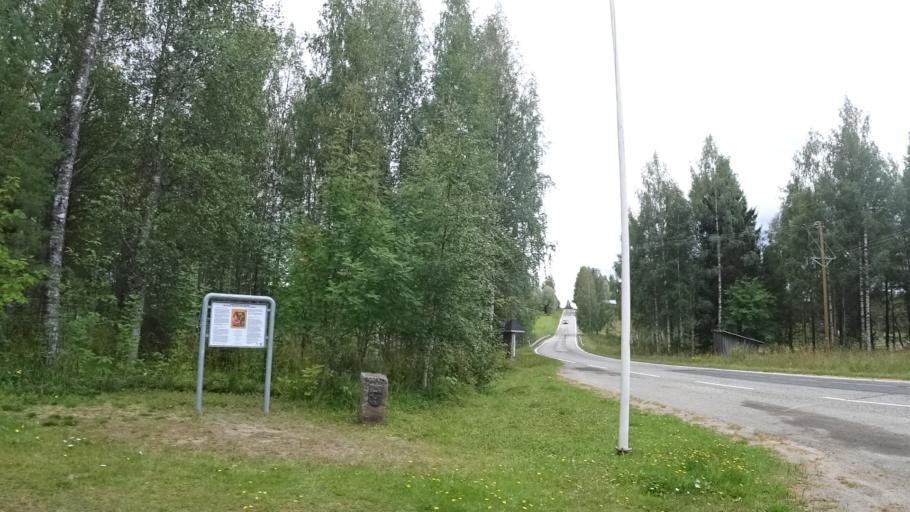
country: FI
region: North Karelia
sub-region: Joensuu
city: Ilomantsi
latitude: 62.4527
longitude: 31.1146
